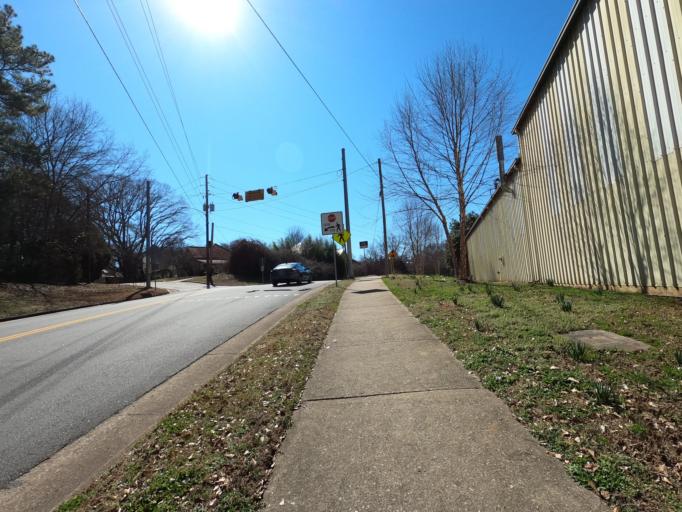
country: US
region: Georgia
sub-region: Clarke County
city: Athens
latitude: 33.9693
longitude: -83.3777
